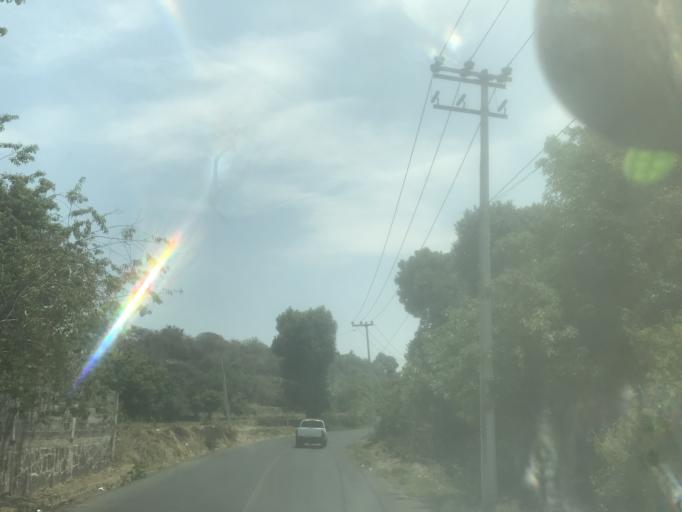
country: MX
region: Mexico
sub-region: Ozumba
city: San Jose Tlacotitlan
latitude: 18.9926
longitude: -98.8044
